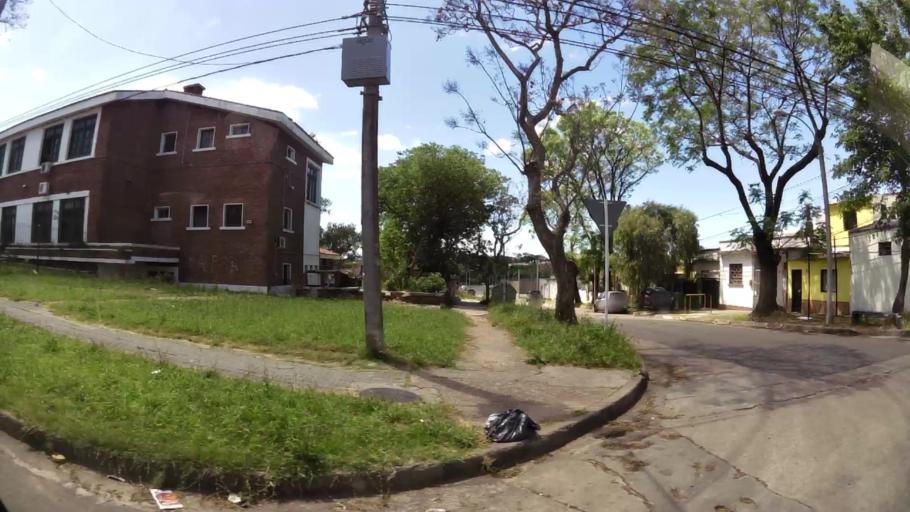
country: UY
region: Montevideo
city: Montevideo
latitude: -34.8578
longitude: -56.1298
